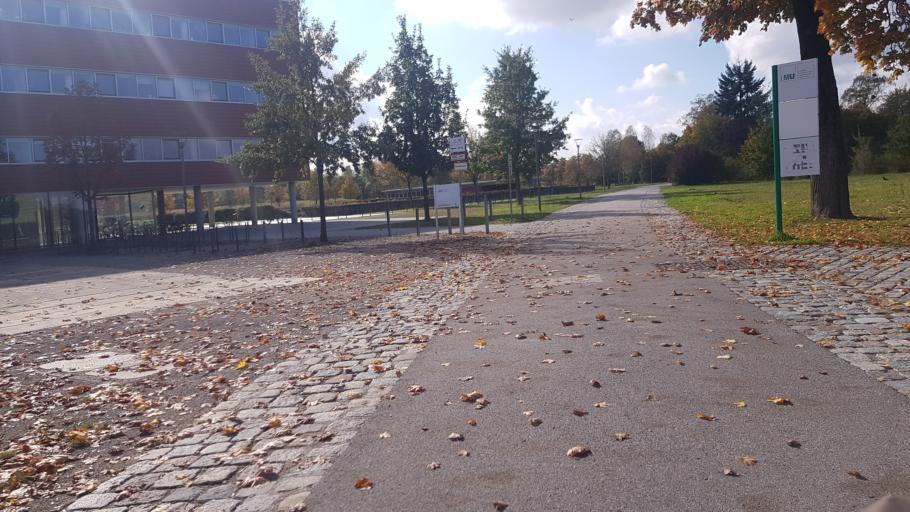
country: DE
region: Bavaria
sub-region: Upper Bavaria
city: Neuried
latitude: 48.1096
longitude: 11.4583
